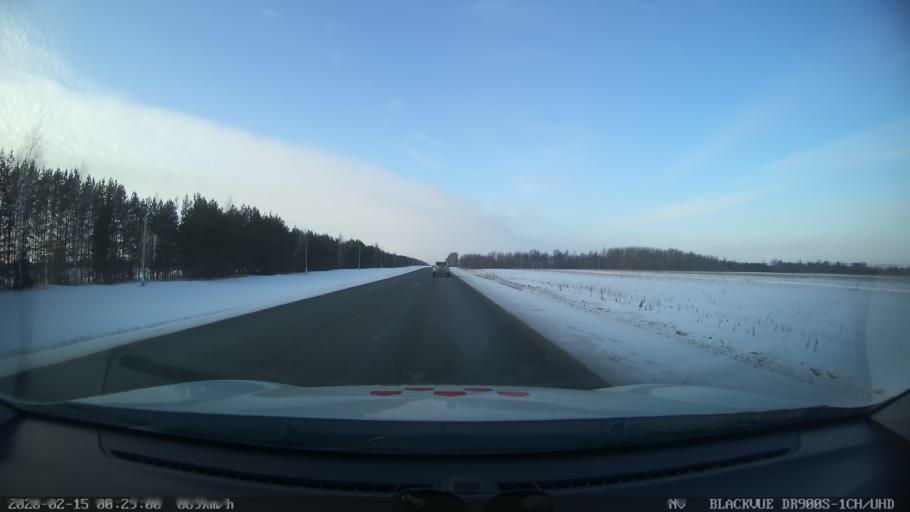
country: RU
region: Tatarstan
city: Verkhniy Uslon
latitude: 55.6469
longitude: 48.8732
